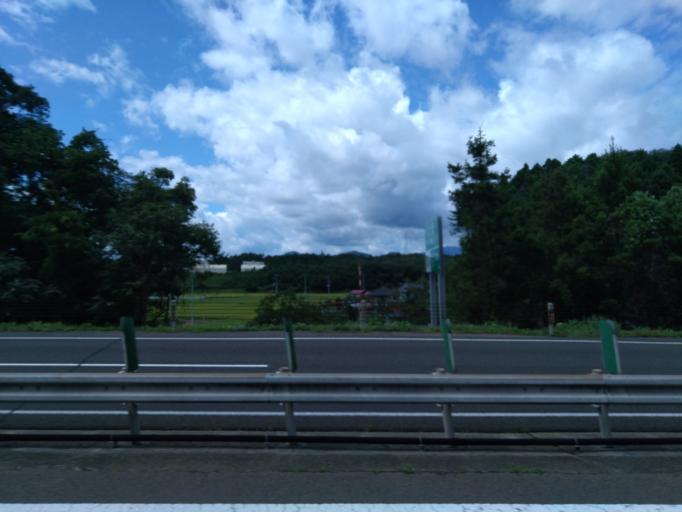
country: JP
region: Miyagi
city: Tomiya
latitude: 38.4526
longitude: 140.9088
